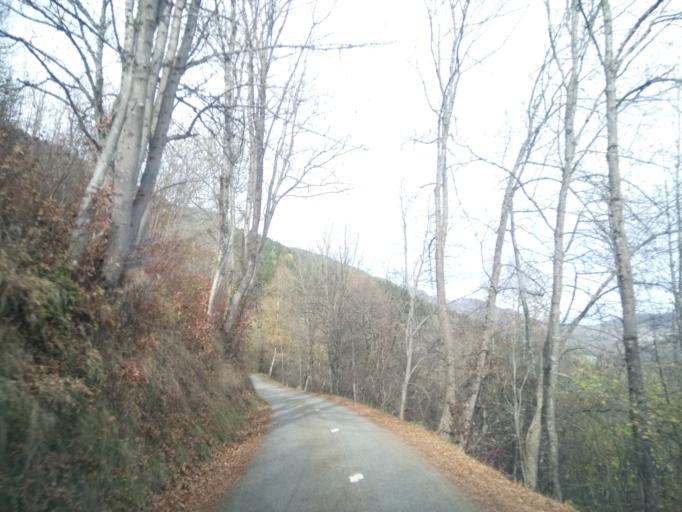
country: FR
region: Rhone-Alpes
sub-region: Departement de la Savoie
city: La Chambre
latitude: 45.3929
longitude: 6.3172
